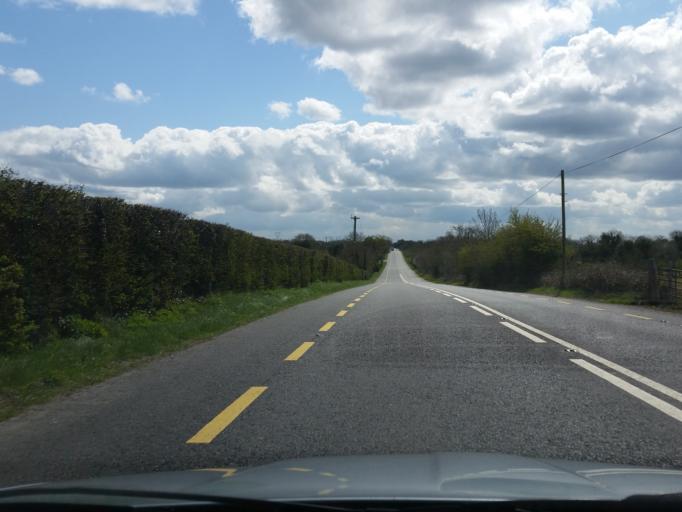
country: IE
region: Leinster
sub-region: An Mhi
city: Slane
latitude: 53.6752
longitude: -6.5365
